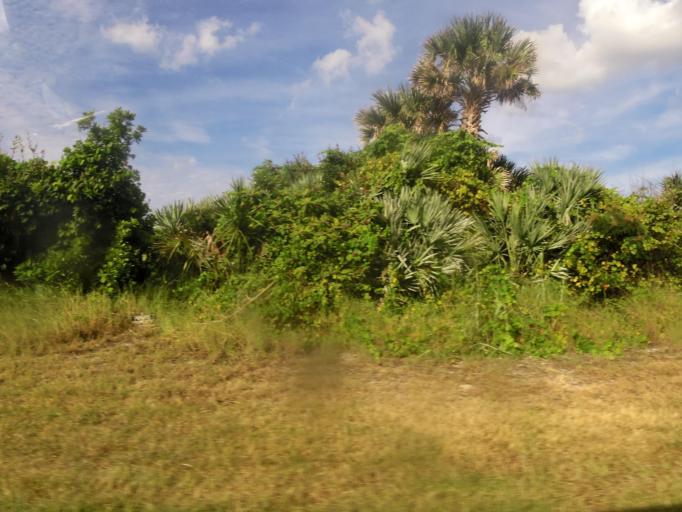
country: US
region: Florida
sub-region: Volusia County
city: Ponce Inlet
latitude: 29.0862
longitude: -80.9274
